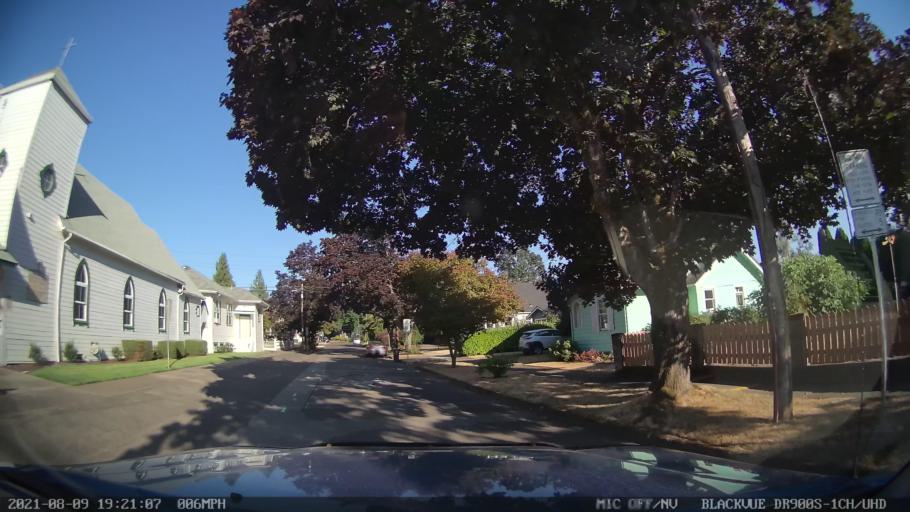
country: US
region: Oregon
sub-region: Marion County
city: Salem
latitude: 44.9416
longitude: -123.0184
